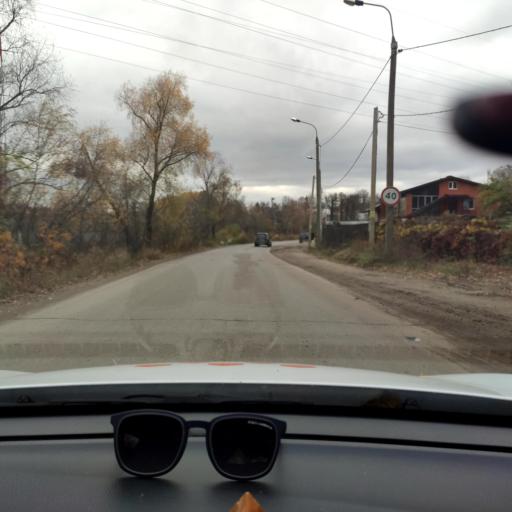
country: RU
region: Tatarstan
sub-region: Gorod Kazan'
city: Kazan
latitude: 55.7249
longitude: 49.1568
